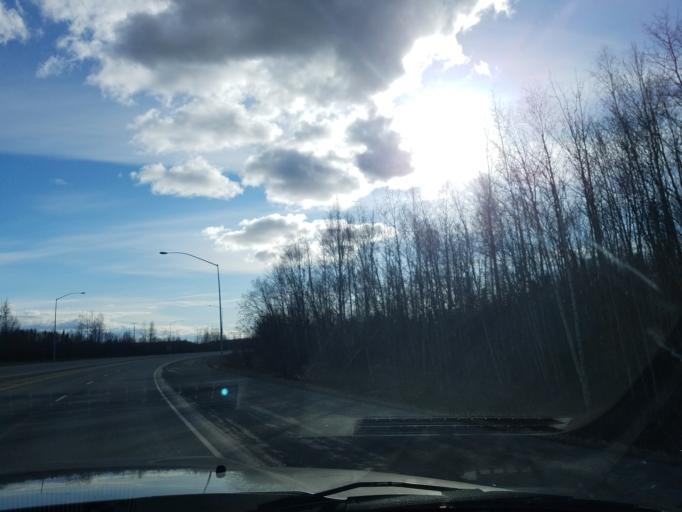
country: US
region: Alaska
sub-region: Anchorage Municipality
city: Elmendorf Air Force Base
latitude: 61.1833
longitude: -149.7360
